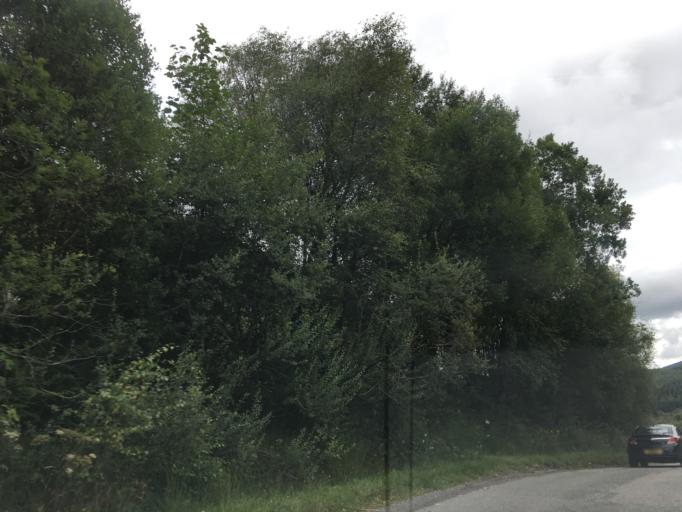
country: GB
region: Scotland
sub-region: Argyll and Bute
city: Oban
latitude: 56.3810
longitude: -5.1848
